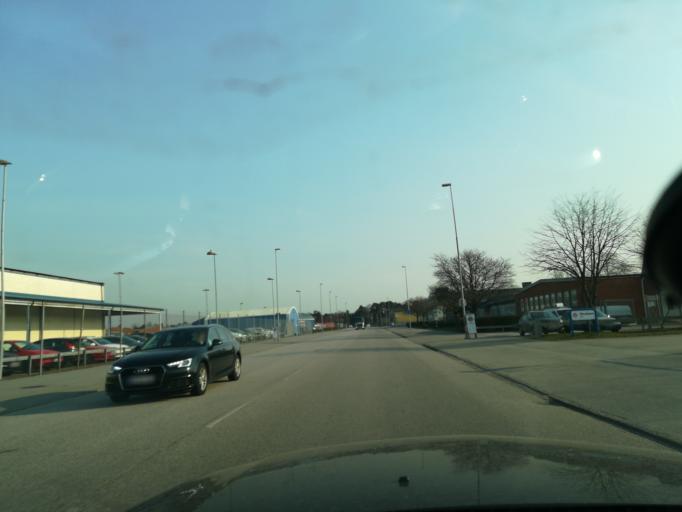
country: SE
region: Skane
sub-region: Ystads Kommun
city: Ystad
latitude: 55.4248
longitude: 13.8392
